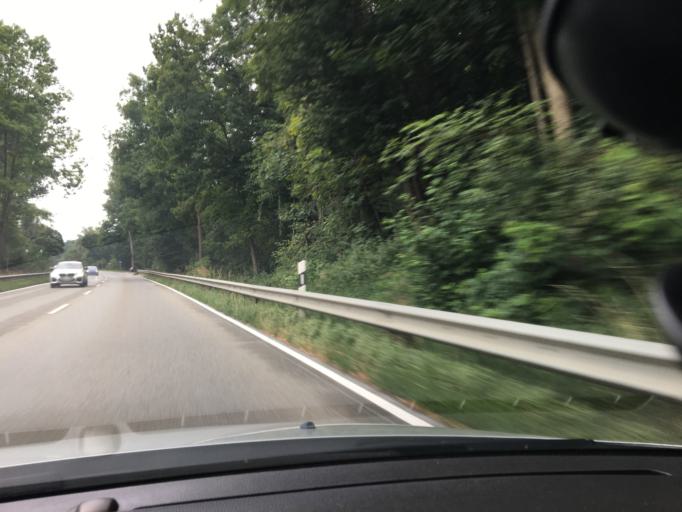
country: DE
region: Bavaria
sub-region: Upper Bavaria
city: Muehldorf
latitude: 48.2432
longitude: 12.5148
